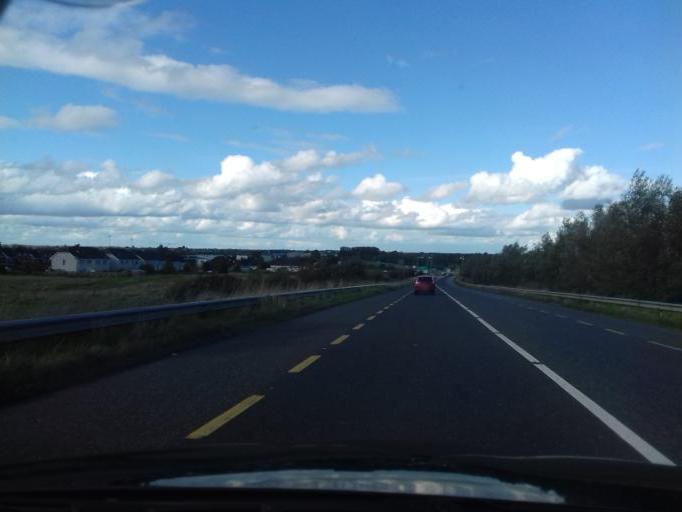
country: IE
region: Leinster
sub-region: Uibh Fhaili
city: Tullamore
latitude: 53.2628
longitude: -7.4648
